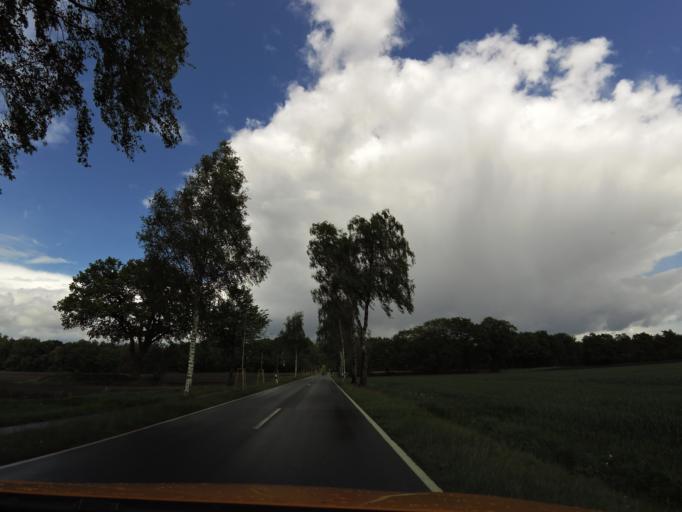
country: DE
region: Lower Saxony
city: Ganderkesee
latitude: 53.0056
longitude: 8.5381
